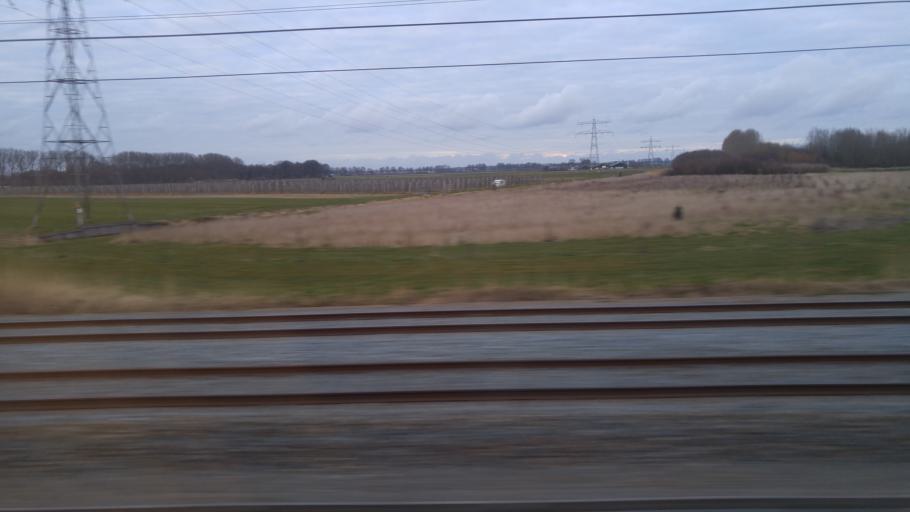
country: NL
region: Utrecht
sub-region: Gemeente Utrecht
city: Lunetten
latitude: 52.0508
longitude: 5.1567
